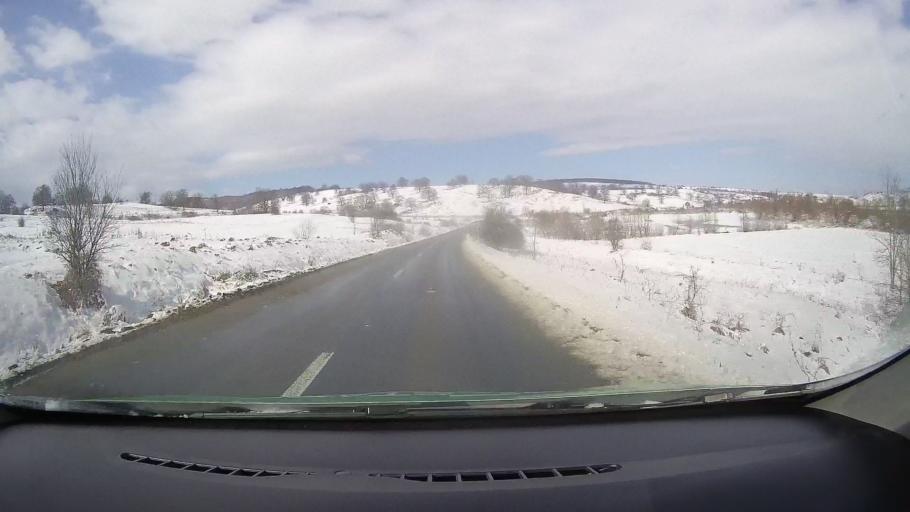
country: RO
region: Sibiu
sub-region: Comuna Altina
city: Altina
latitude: 45.9440
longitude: 24.4524
